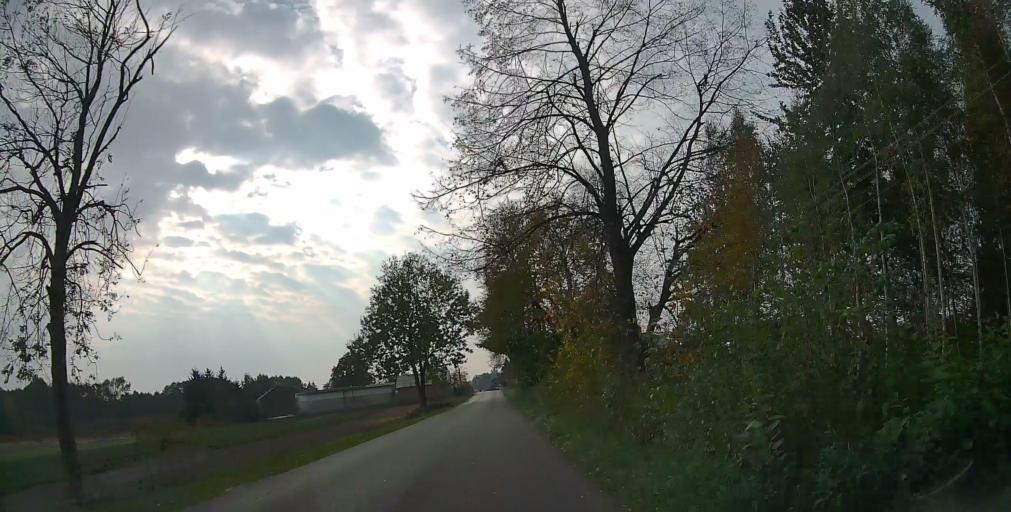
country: PL
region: Masovian Voivodeship
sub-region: Powiat grojecki
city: Mogielnica
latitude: 51.6635
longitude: 20.7103
